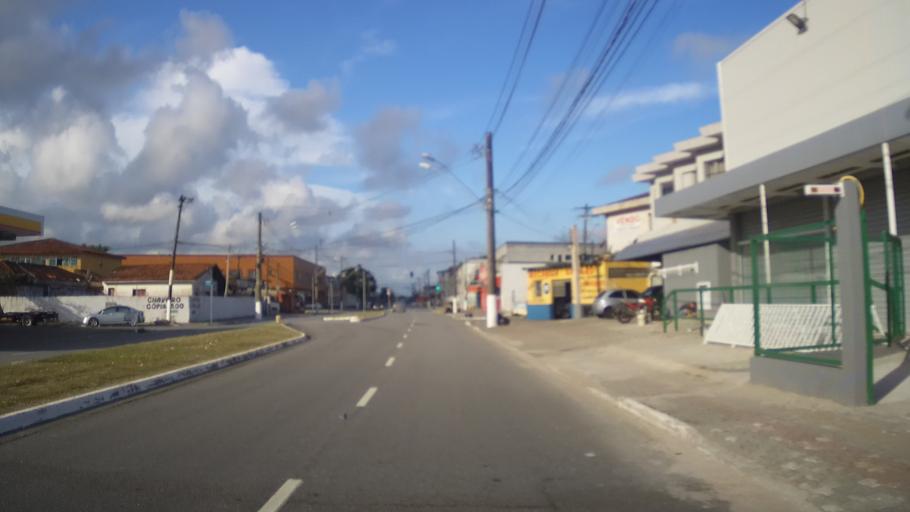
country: BR
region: Sao Paulo
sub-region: Mongagua
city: Mongagua
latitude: -24.0631
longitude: -46.5625
